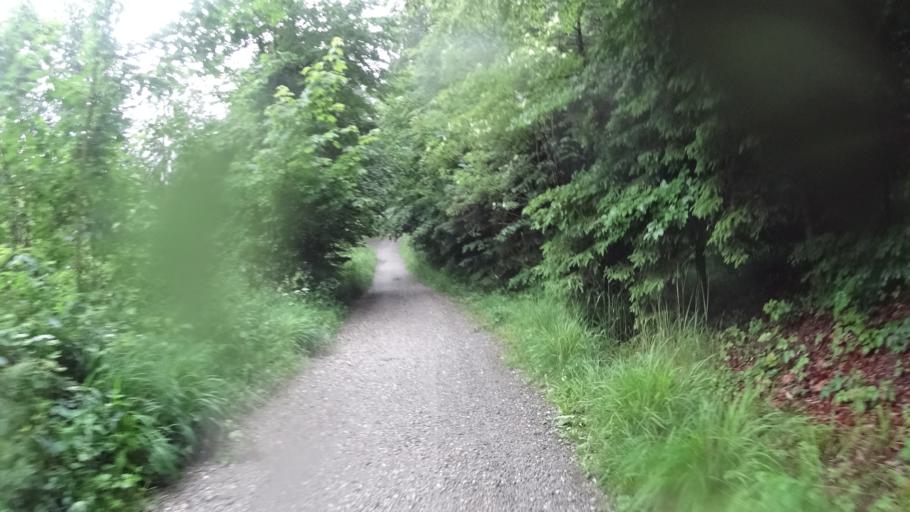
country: AT
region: Upper Austria
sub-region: Politischer Bezirk Scharding
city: Scharding
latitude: 48.4931
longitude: 13.4458
